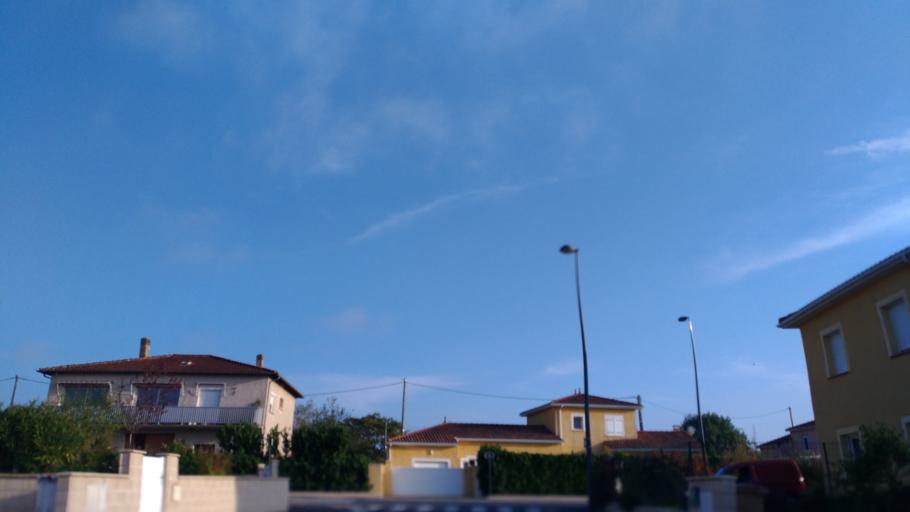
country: FR
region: Midi-Pyrenees
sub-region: Departement du Tarn
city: Puygouzon
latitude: 43.9151
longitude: 2.1755
